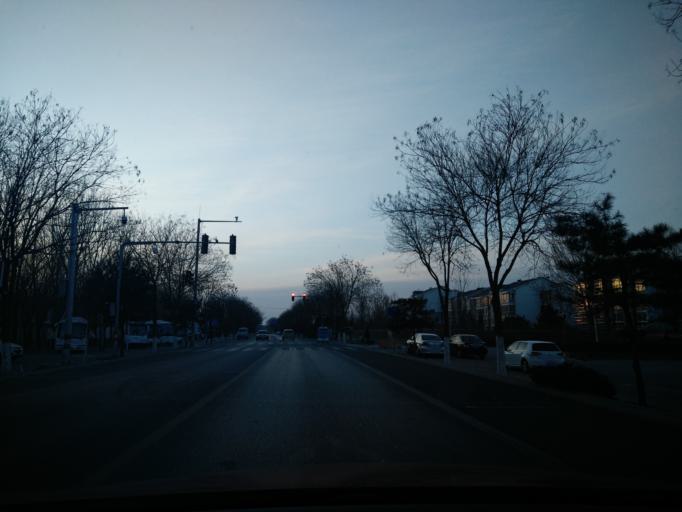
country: CN
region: Beijing
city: Qingyundian
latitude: 39.6726
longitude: 116.5217
